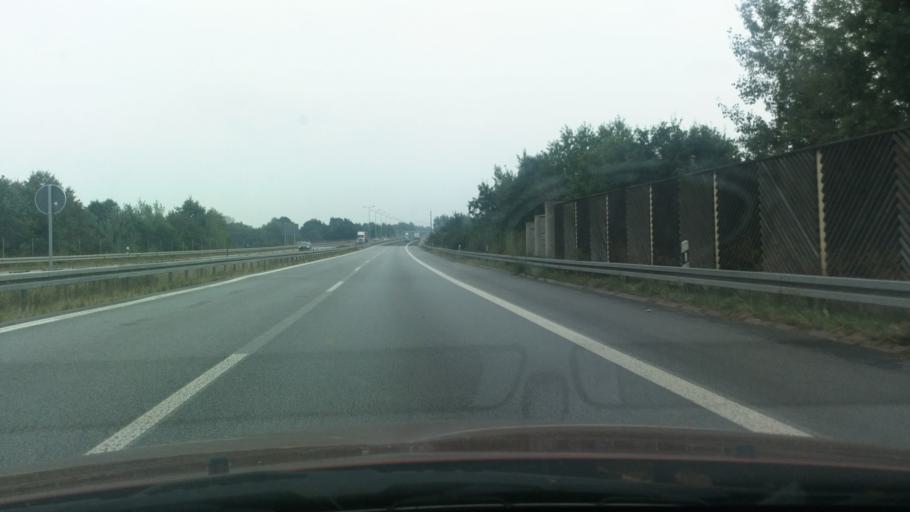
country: DE
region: Saxony
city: Goerlitz
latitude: 51.1829
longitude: 15.0025
